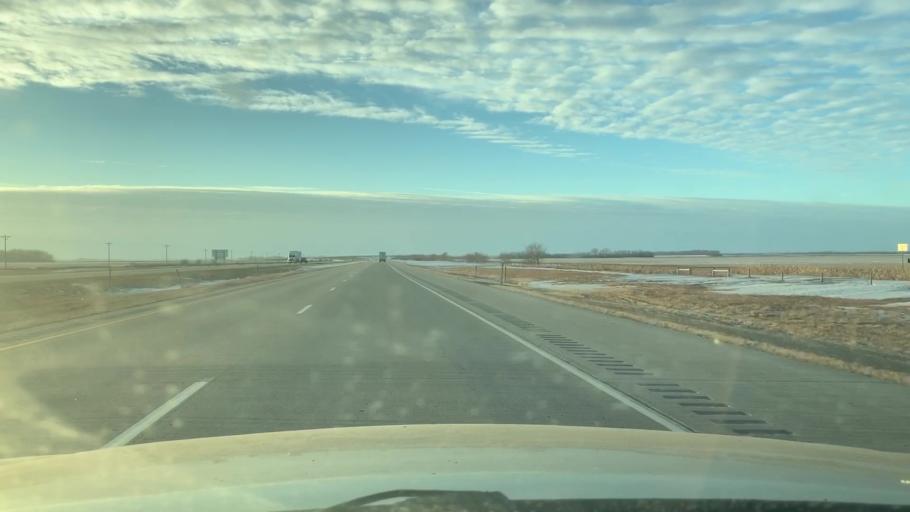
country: US
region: North Dakota
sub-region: Cass County
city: Casselton
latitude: 46.8759
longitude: -97.3238
